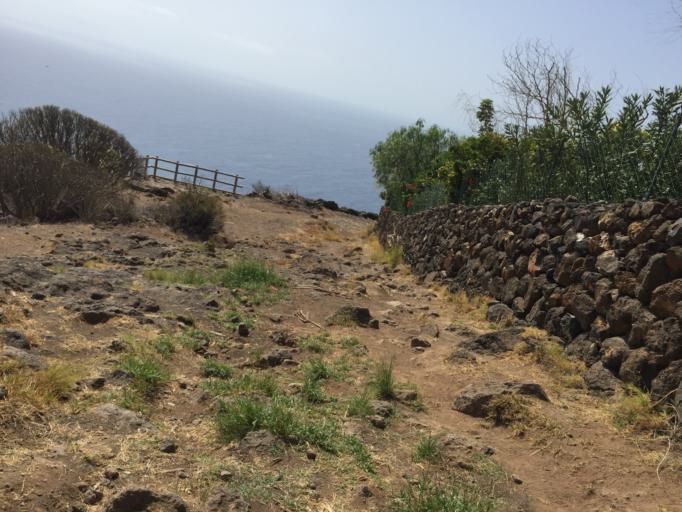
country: ES
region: Canary Islands
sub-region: Provincia de Santa Cruz de Tenerife
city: Tazacorte
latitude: 28.6542
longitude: -17.9489
